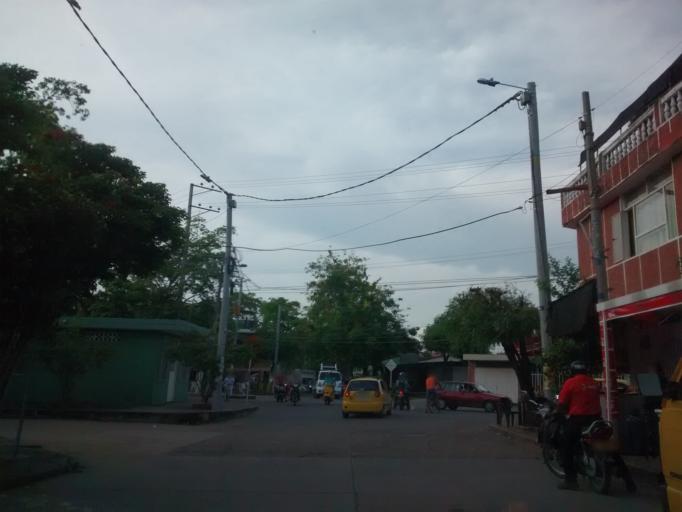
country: CO
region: Cundinamarca
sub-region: Girardot
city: Girardot City
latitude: 4.3031
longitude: -74.8018
